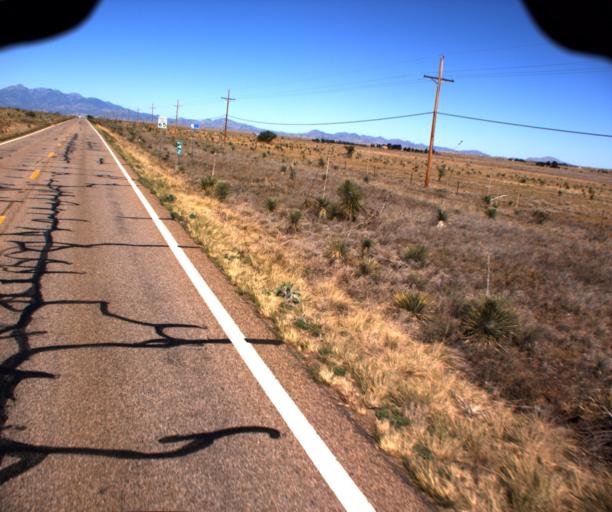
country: US
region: Arizona
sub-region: Cochise County
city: Huachuca City
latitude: 31.7240
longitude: -110.5041
